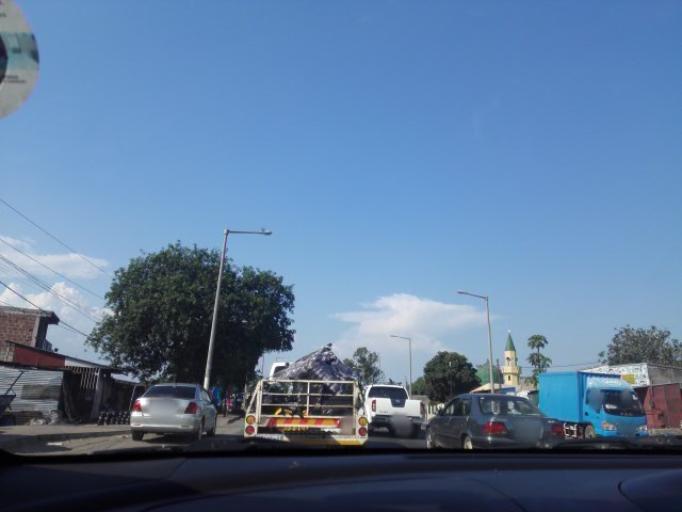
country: MZ
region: Maputo City
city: Maputo
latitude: -25.8846
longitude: 32.5665
